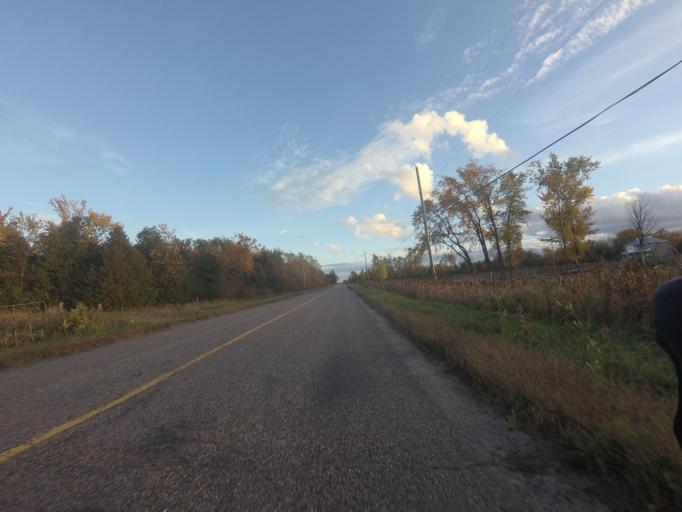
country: CA
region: Ontario
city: Renfrew
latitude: 45.4431
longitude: -76.9661
